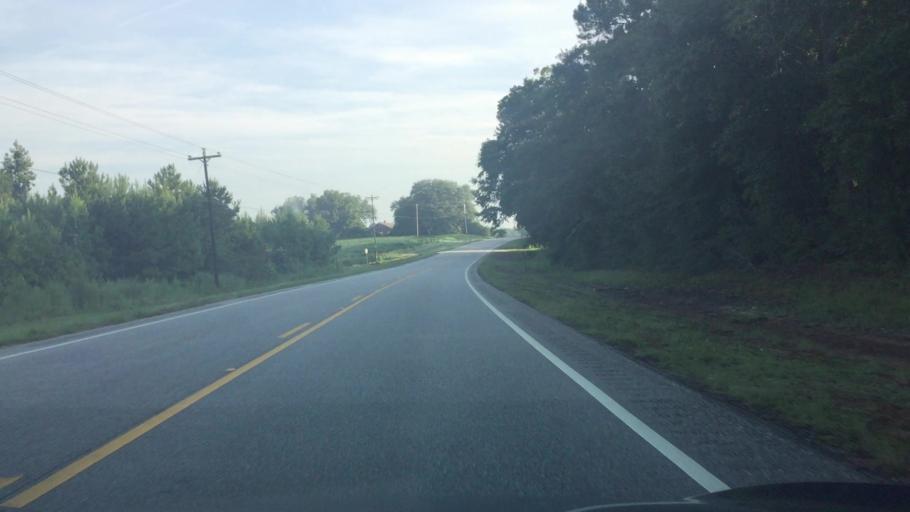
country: US
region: Alabama
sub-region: Covington County
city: Andalusia
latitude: 31.1671
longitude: -86.4601
